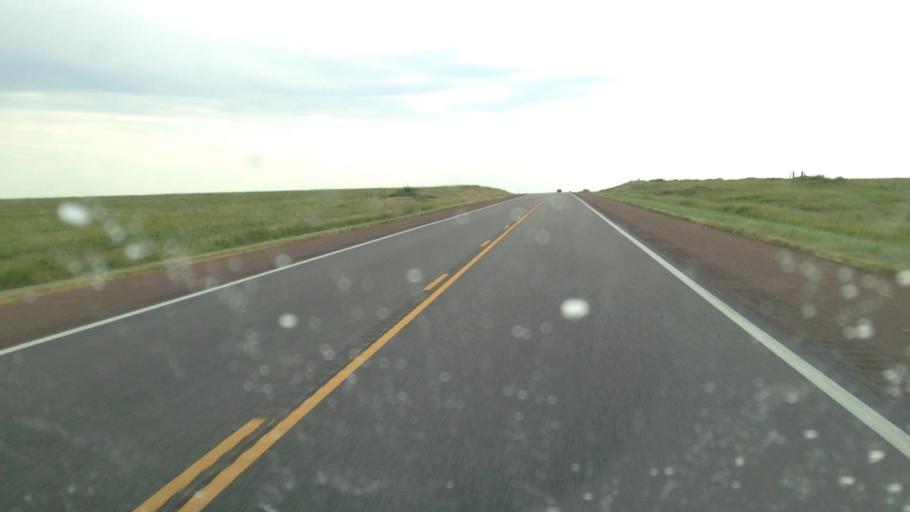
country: US
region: Kansas
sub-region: Coffey County
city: Burlington
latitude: 38.0599
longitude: -95.7391
